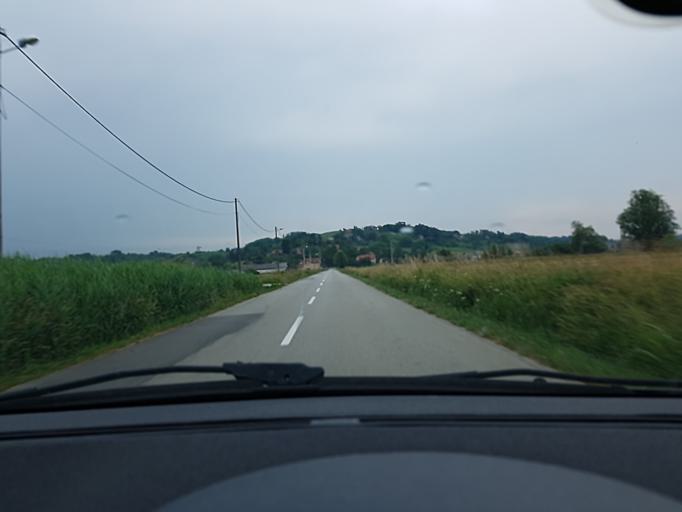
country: HR
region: Zagrebacka
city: Jakovlje
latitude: 45.9487
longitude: 15.8124
